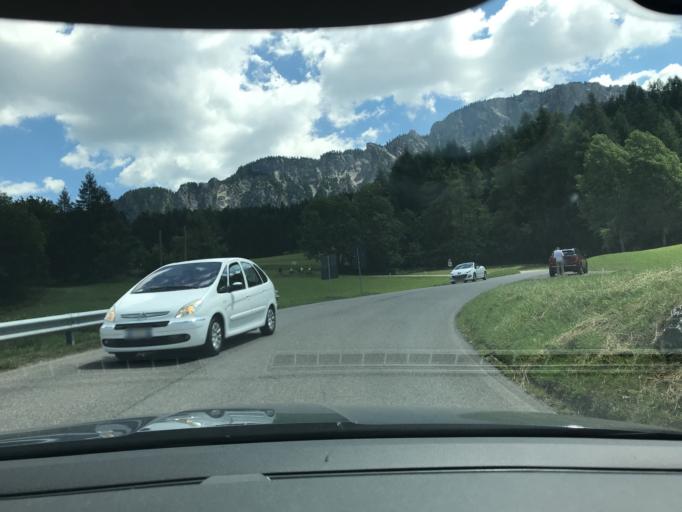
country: IT
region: Veneto
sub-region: Provincia di Belluno
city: Cortina d'Ampezzo
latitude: 46.5430
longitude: 12.1522
